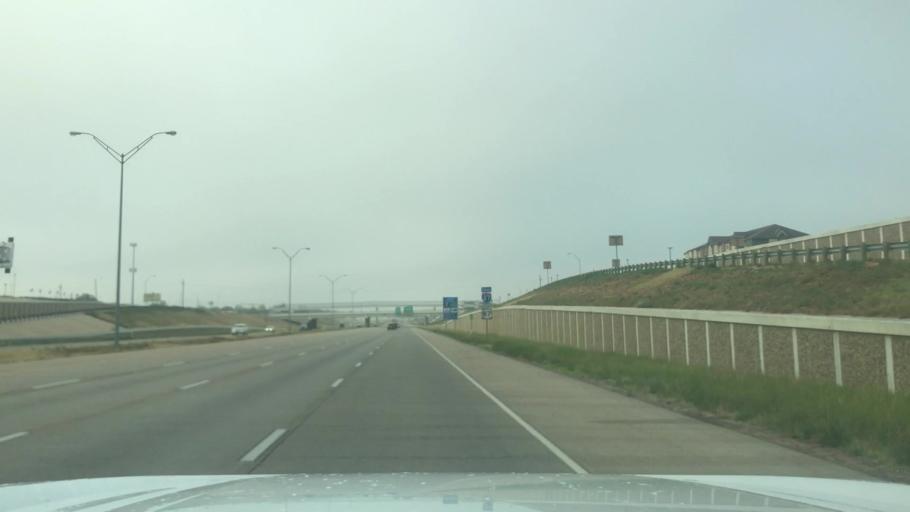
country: US
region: Texas
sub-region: Lubbock County
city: Lubbock
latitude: 33.5530
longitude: -101.8453
